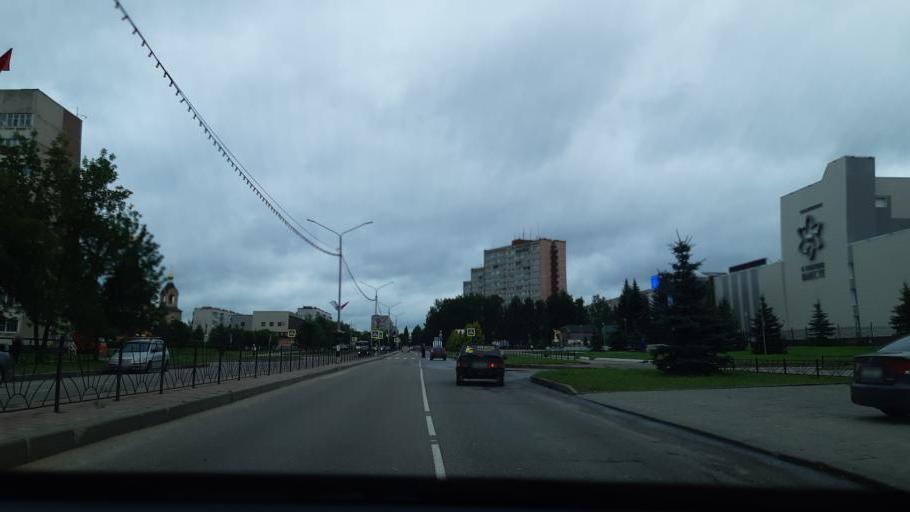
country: RU
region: Smolensk
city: Desnogorsk
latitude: 54.1504
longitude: 33.2860
